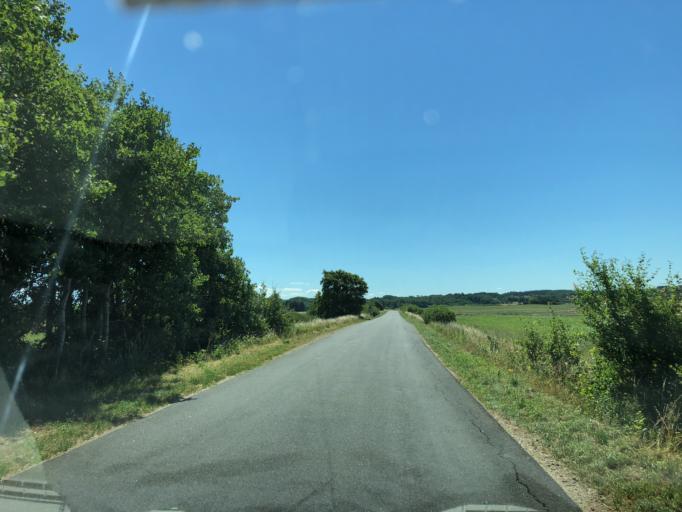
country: DK
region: Central Jutland
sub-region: Viborg Kommune
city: Viborg
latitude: 56.5506
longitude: 9.4330
